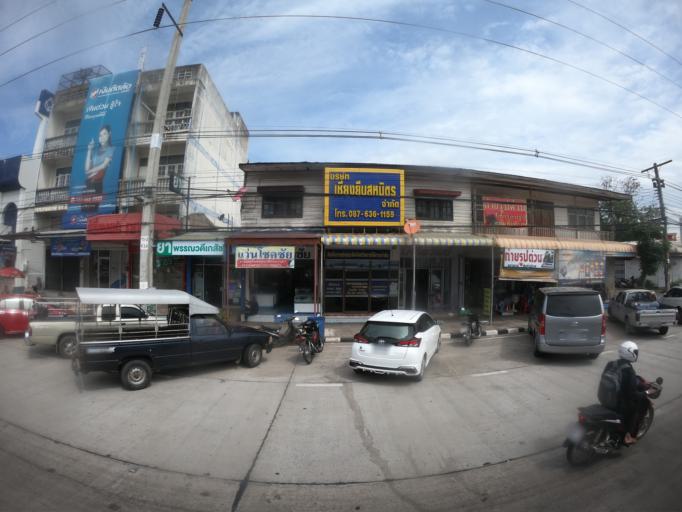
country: TH
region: Maha Sarakham
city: Chiang Yuen
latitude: 16.4105
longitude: 103.0969
